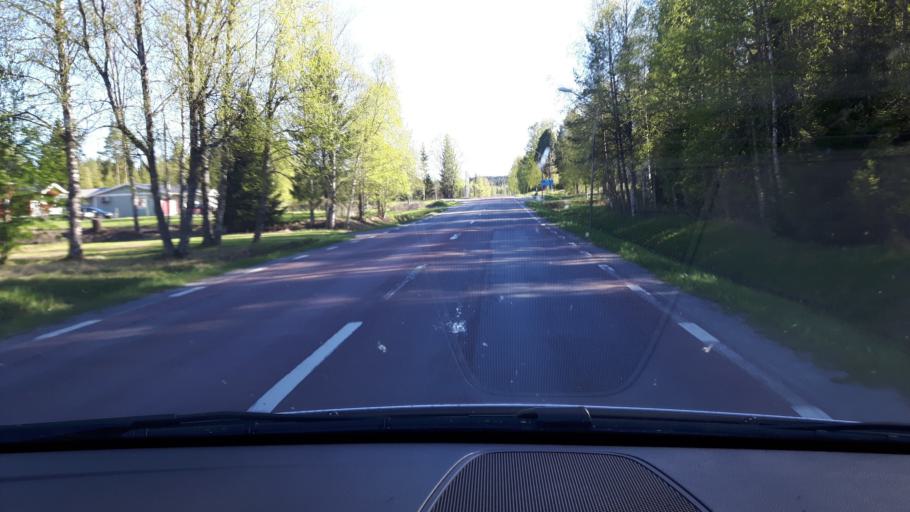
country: SE
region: Jaemtland
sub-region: Stroemsunds Kommun
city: Stroemsund
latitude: 63.8397
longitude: 15.5235
